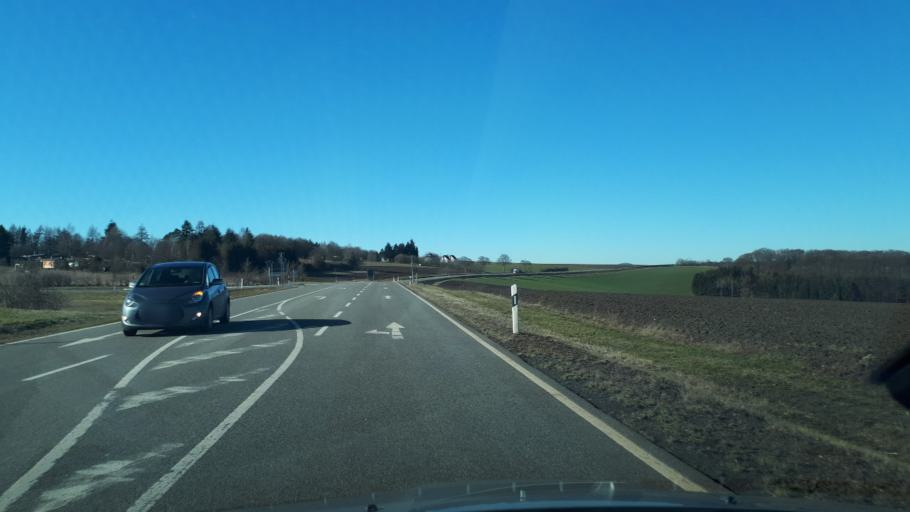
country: DE
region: Rheinland-Pfalz
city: Immerath
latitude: 50.1326
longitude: 6.9384
